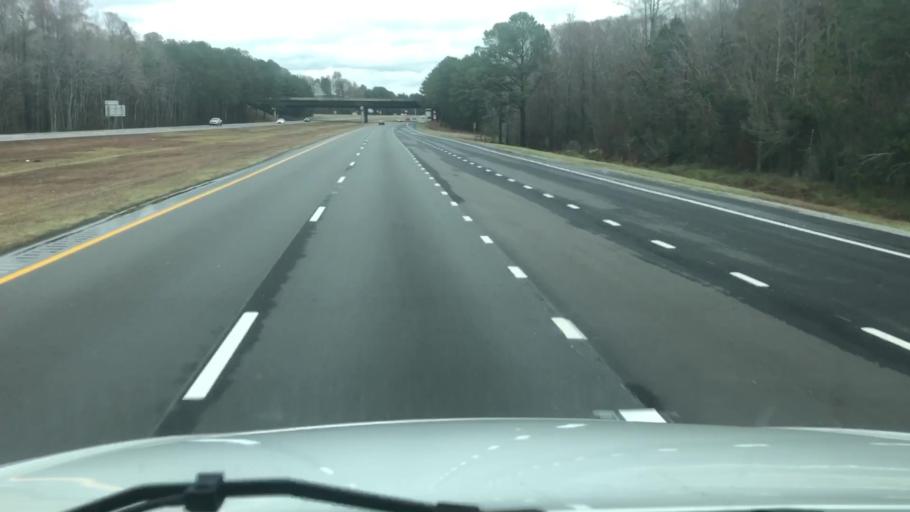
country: US
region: North Carolina
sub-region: Cumberland County
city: Eastover
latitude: 35.0857
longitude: -78.7848
